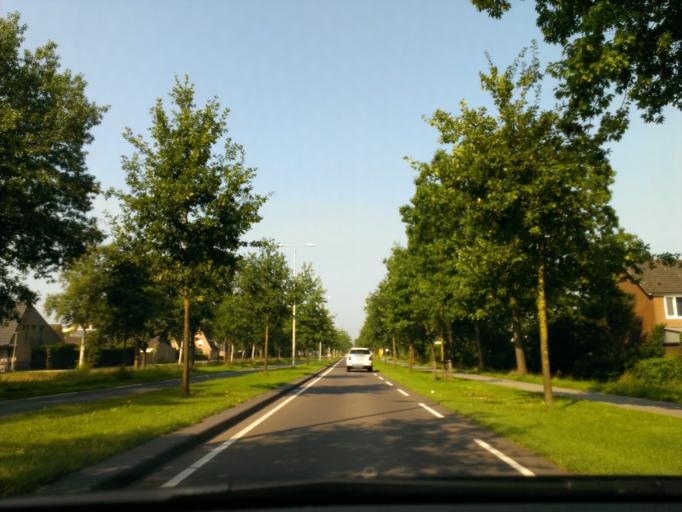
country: NL
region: Drenthe
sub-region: Gemeente Hoogeveen
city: Hoogeveen
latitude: 52.7206
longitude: 6.5115
